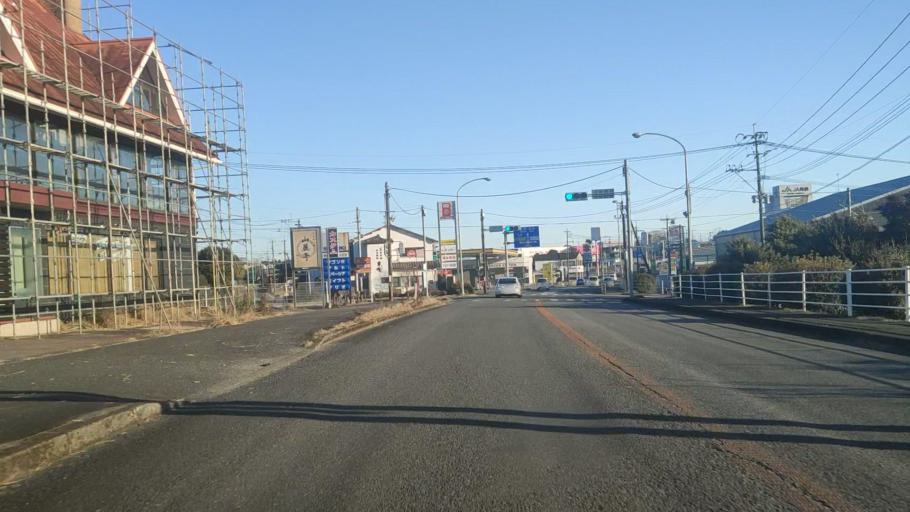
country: JP
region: Miyazaki
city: Takanabe
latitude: 32.1953
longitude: 131.5248
